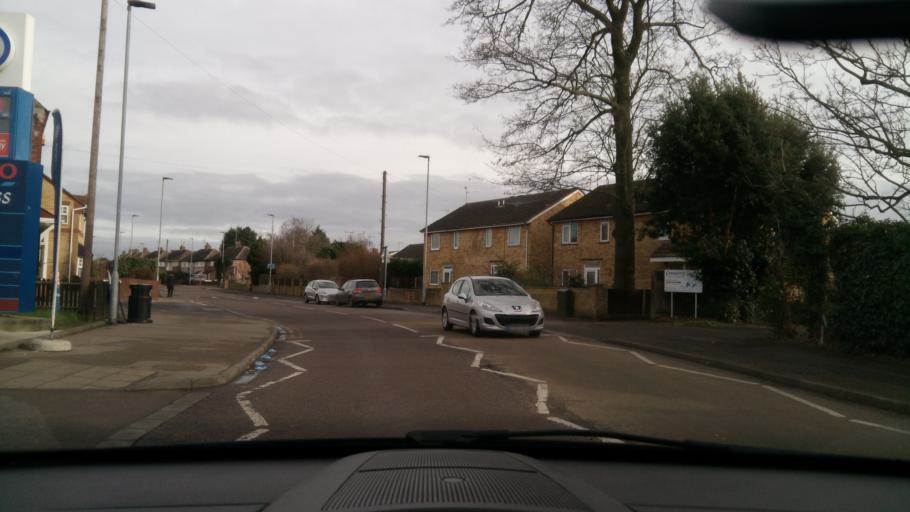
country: GB
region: England
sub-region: Peterborough
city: Peterborough
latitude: 52.5963
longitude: -0.2405
